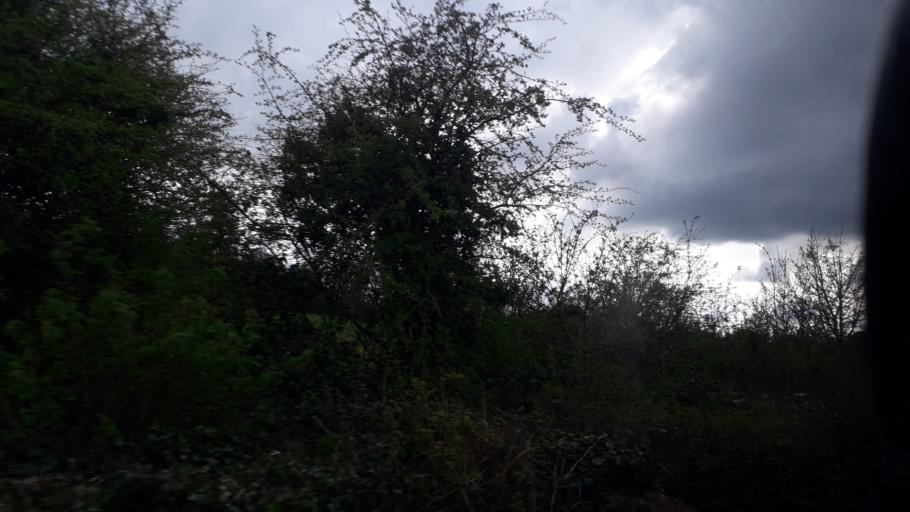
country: IE
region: Leinster
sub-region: An Iarmhi
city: Rathwire
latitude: 53.4948
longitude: -7.1787
